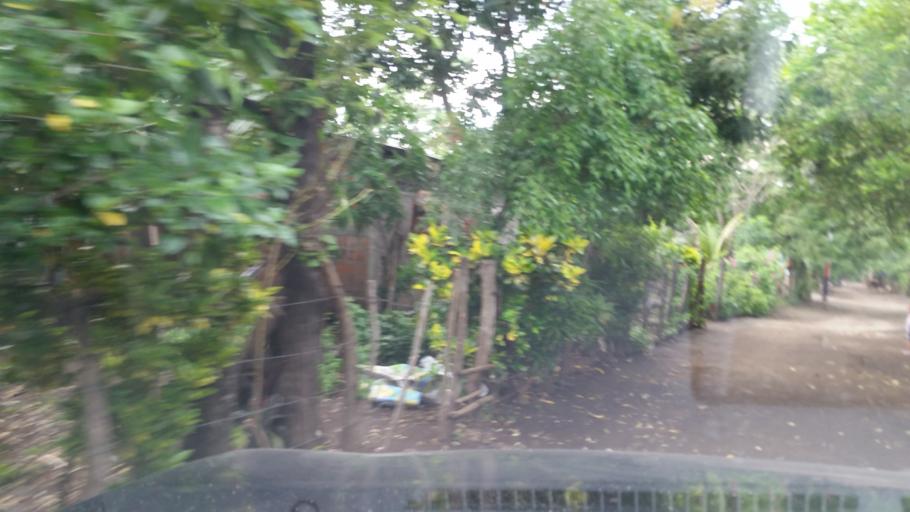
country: NI
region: Chinandega
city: Puerto Morazan
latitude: 12.7639
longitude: -87.1270
